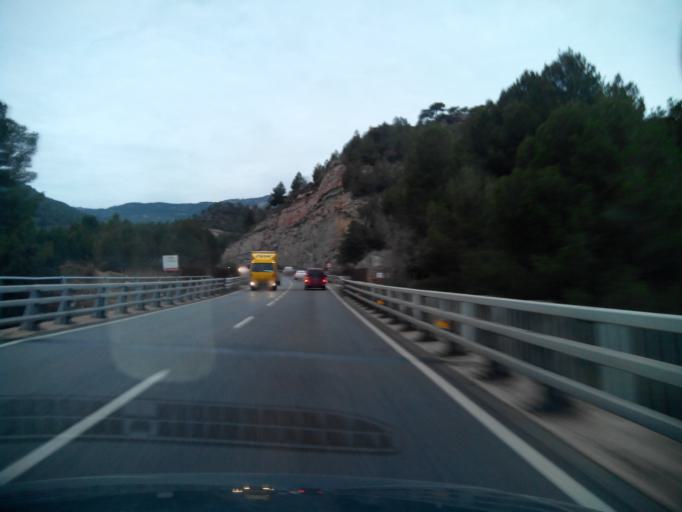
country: ES
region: Catalonia
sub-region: Provincia de Barcelona
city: Monistrol de Montserrat
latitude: 41.6233
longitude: 1.8542
